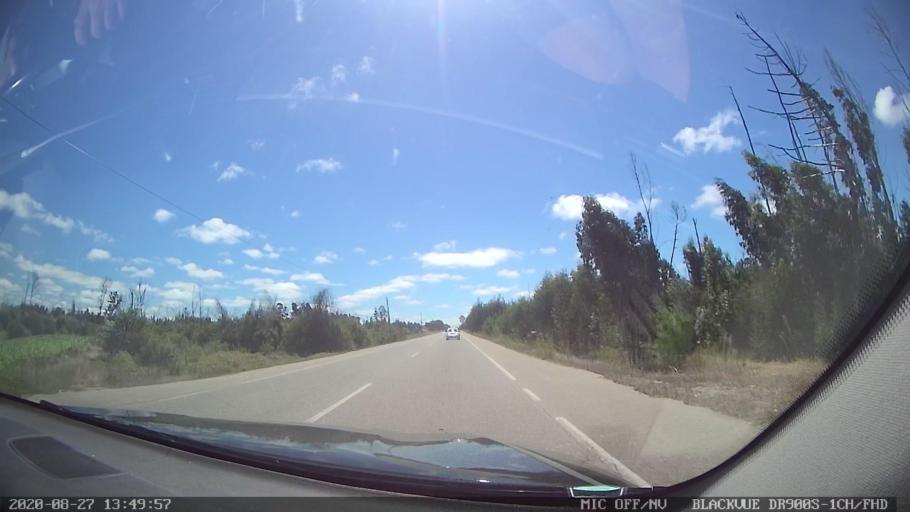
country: PT
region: Coimbra
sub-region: Mira
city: Mira
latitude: 40.3623
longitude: -8.7470
